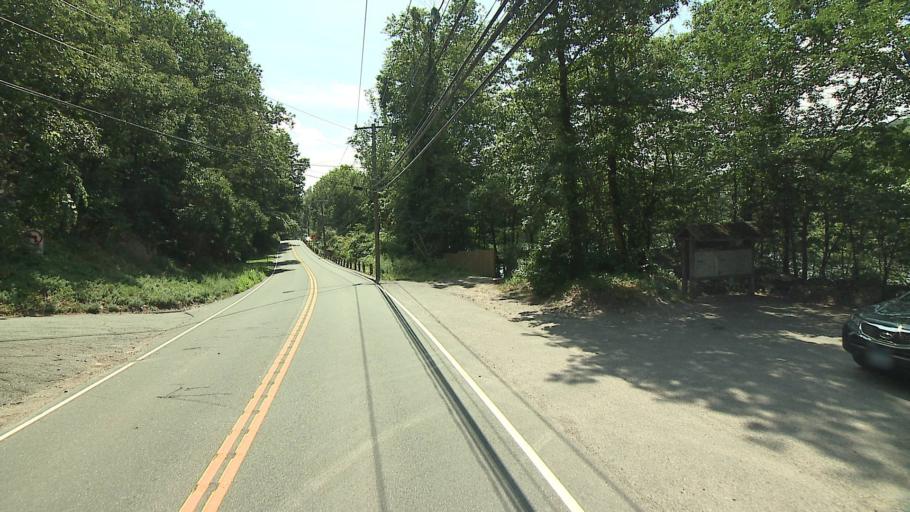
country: US
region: Connecticut
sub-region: Fairfield County
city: Sherman
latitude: 41.5131
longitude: -73.4727
